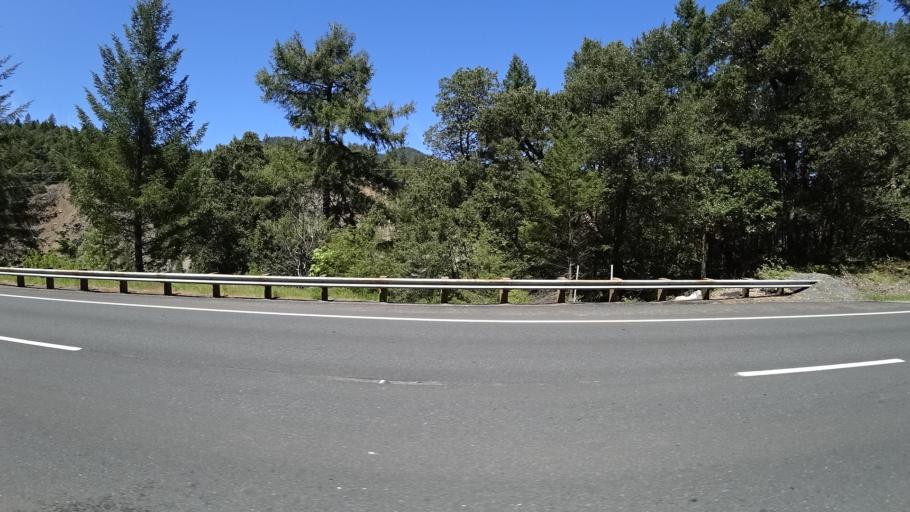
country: US
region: California
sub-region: Humboldt County
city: Willow Creek
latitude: 40.9437
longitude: -123.6641
